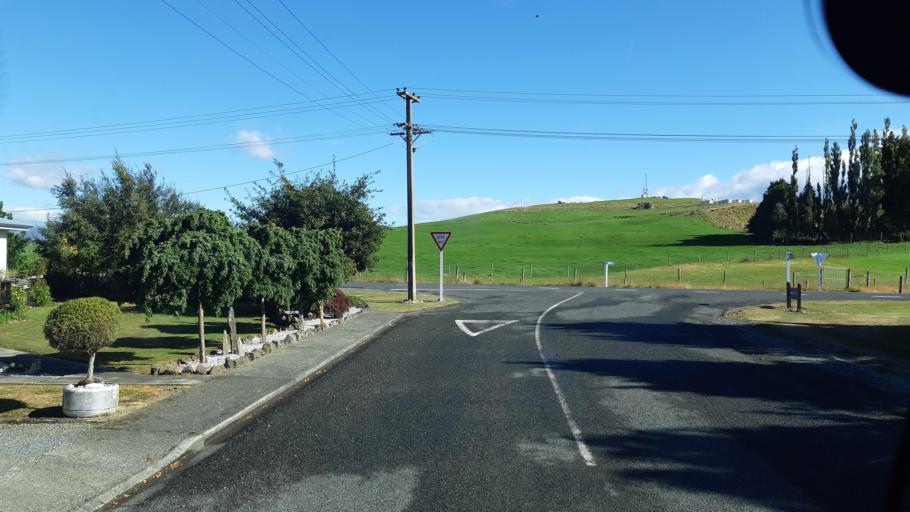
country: NZ
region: Southland
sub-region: Southland District
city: Winton
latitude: -45.6696
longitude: 168.2324
